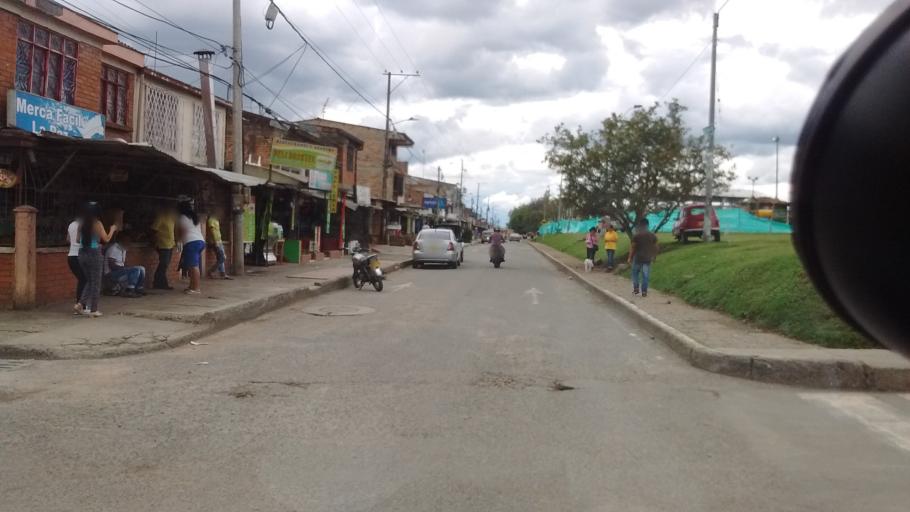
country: CO
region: Cauca
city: Popayan
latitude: 2.4753
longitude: -76.5588
